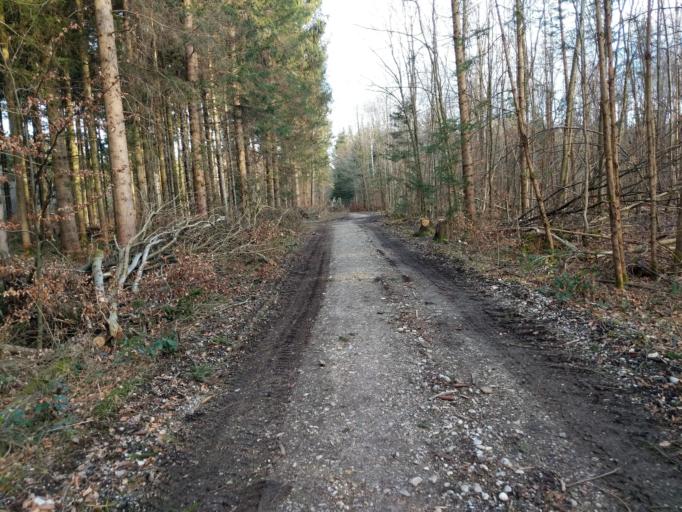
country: DE
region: Bavaria
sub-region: Upper Bavaria
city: Zorneding
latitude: 48.0977
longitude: 11.8439
